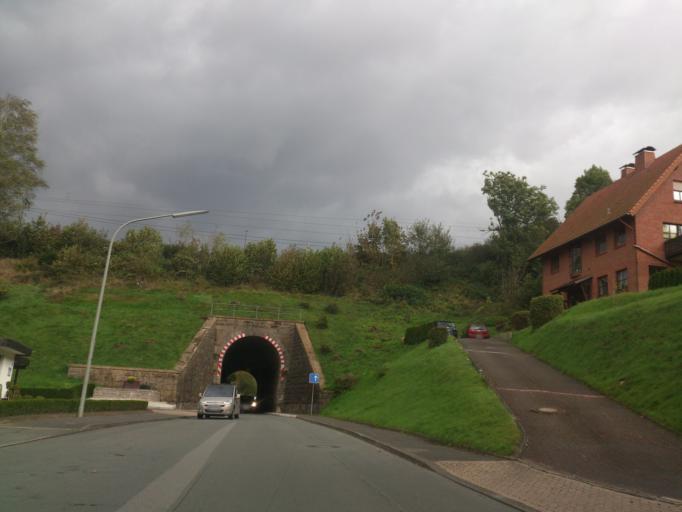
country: DE
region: North Rhine-Westphalia
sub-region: Regierungsbezirk Detmold
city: Altenbeken
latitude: 51.7613
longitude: 8.9522
